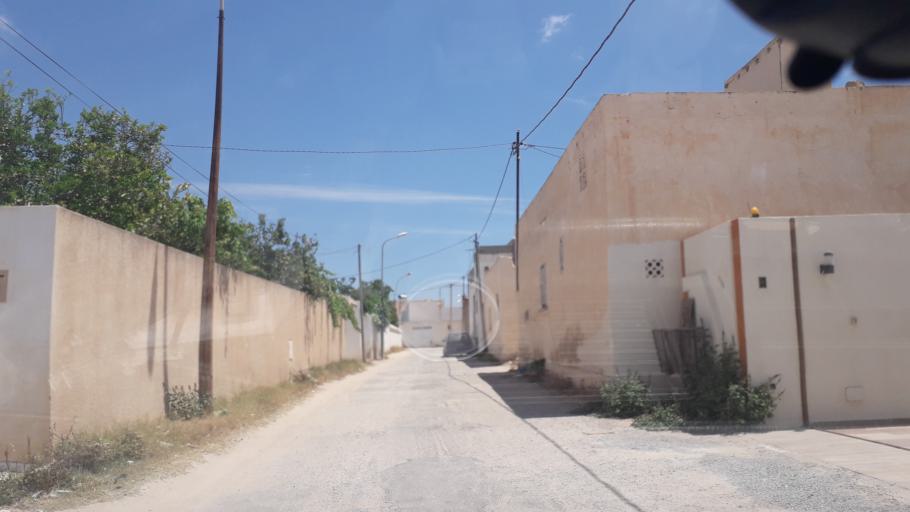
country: TN
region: Safaqis
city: Al Qarmadah
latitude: 34.8168
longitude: 10.7658
